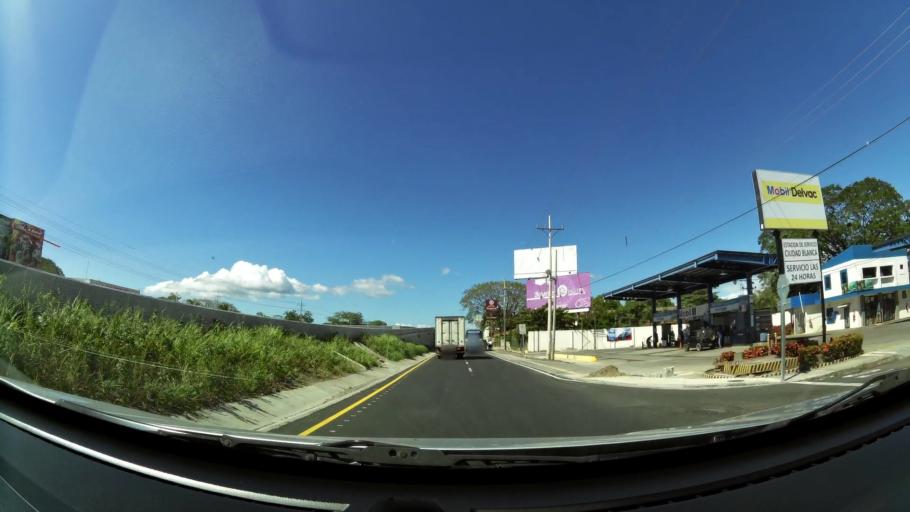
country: CR
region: Guanacaste
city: Liberia
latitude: 10.6246
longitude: -85.4422
